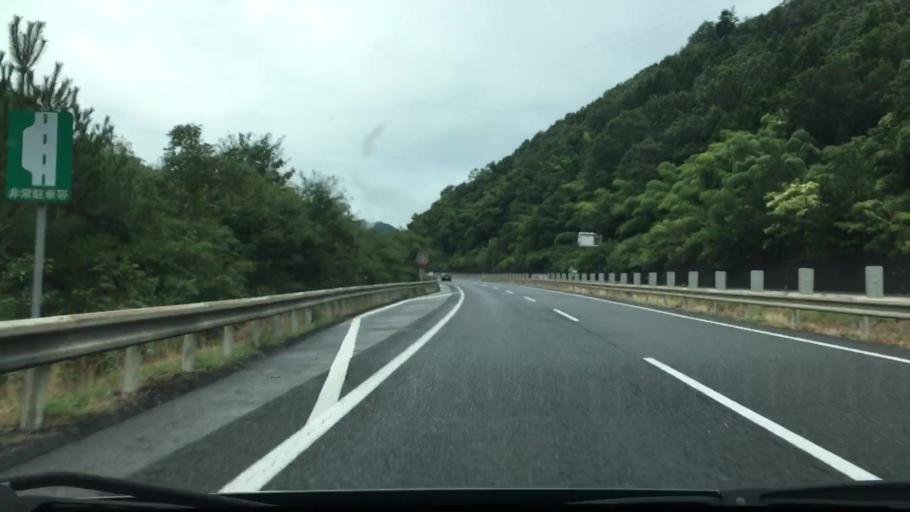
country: JP
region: Hiroshima
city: Hiroshima-shi
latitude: 34.5242
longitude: 132.4294
